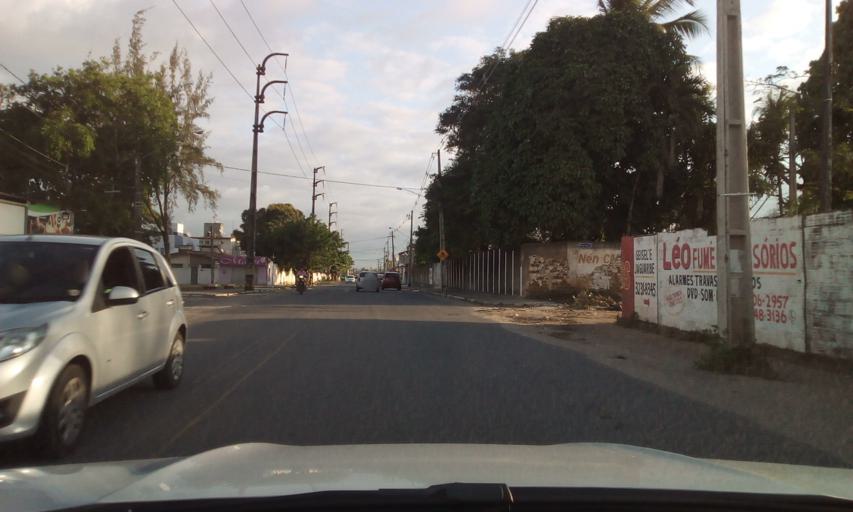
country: BR
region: Paraiba
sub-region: Joao Pessoa
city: Joao Pessoa
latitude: -7.1823
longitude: -34.8737
